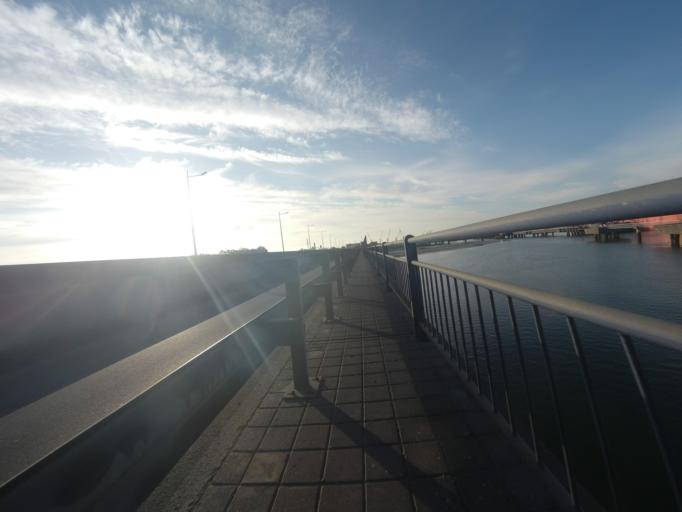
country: ES
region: Andalusia
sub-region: Provincia de Huelva
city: Punta Umbria
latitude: 37.2074
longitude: -6.9373
